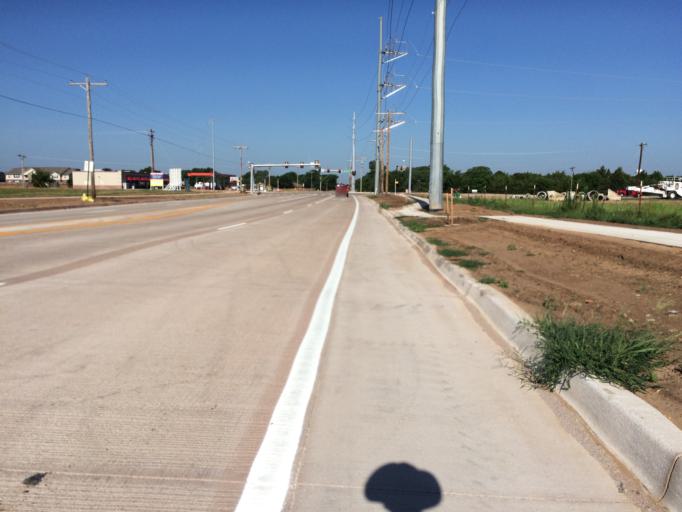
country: US
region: Oklahoma
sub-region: Cleveland County
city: Noble
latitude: 35.1752
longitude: -97.4222
